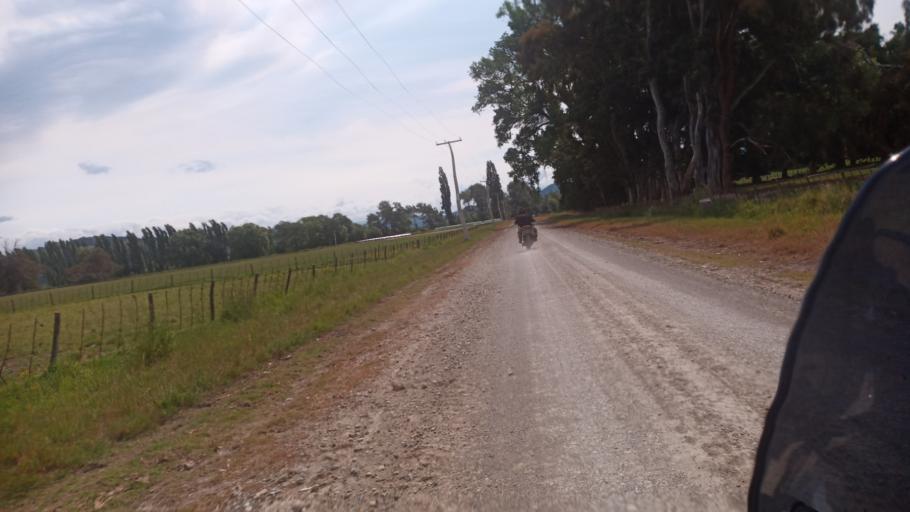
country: NZ
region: Gisborne
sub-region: Gisborne District
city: Gisborne
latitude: -38.4678
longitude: 177.8499
